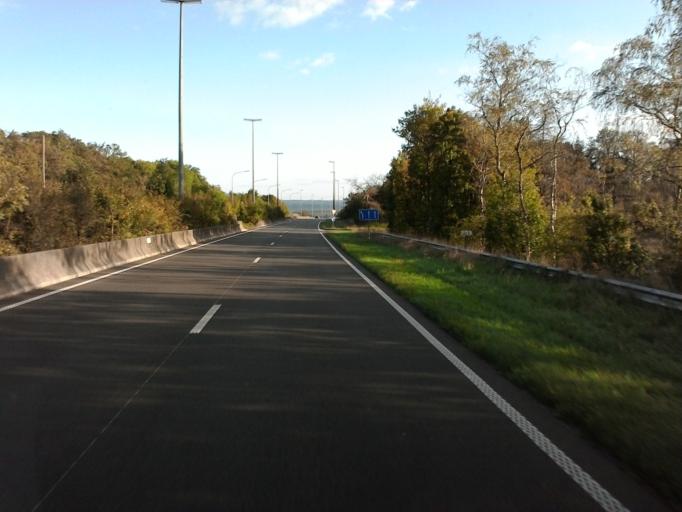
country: BE
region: Wallonia
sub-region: Province de Namur
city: Somme-Leuze
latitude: 50.3024
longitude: 5.3479
